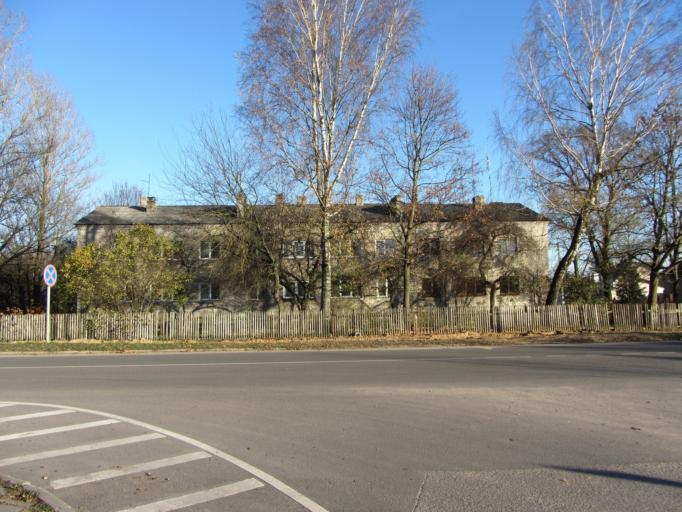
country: LT
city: Eisiskes
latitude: 54.1805
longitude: 24.9988
